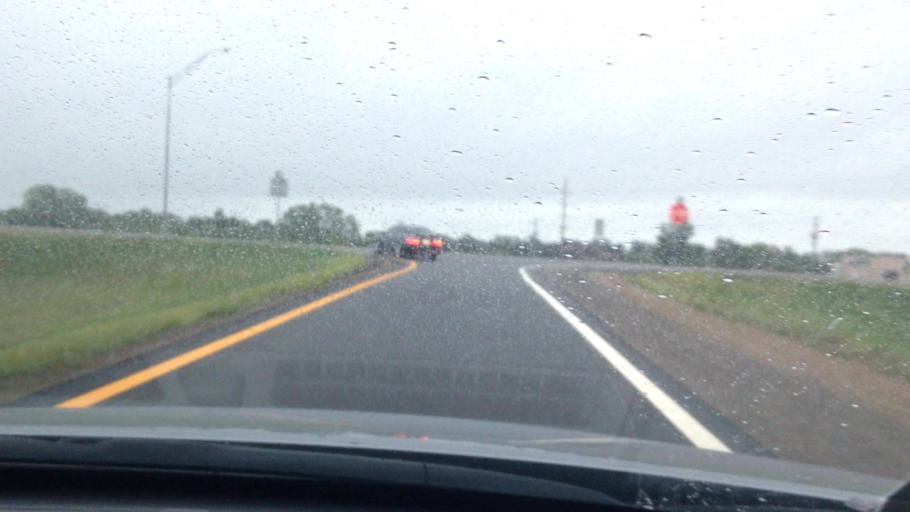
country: US
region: Kansas
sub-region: Brown County
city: Hiawatha
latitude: 39.8399
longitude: -95.5278
